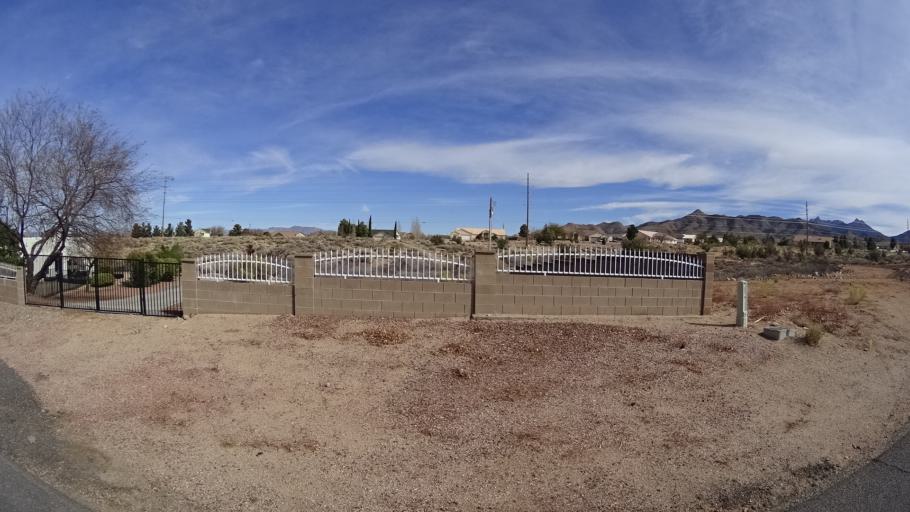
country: US
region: Arizona
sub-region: Mohave County
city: Kingman
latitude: 35.1868
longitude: -113.9856
